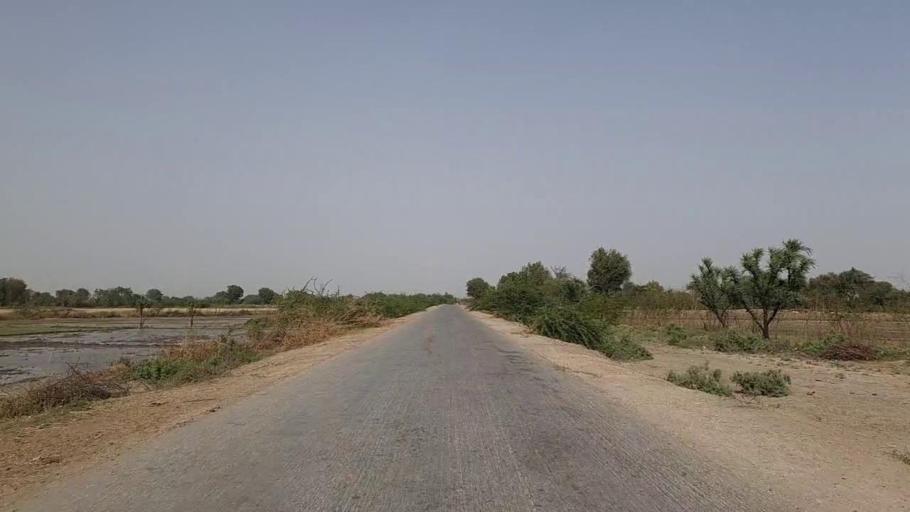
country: PK
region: Sindh
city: Tando Bago
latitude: 24.8981
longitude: 69.0800
